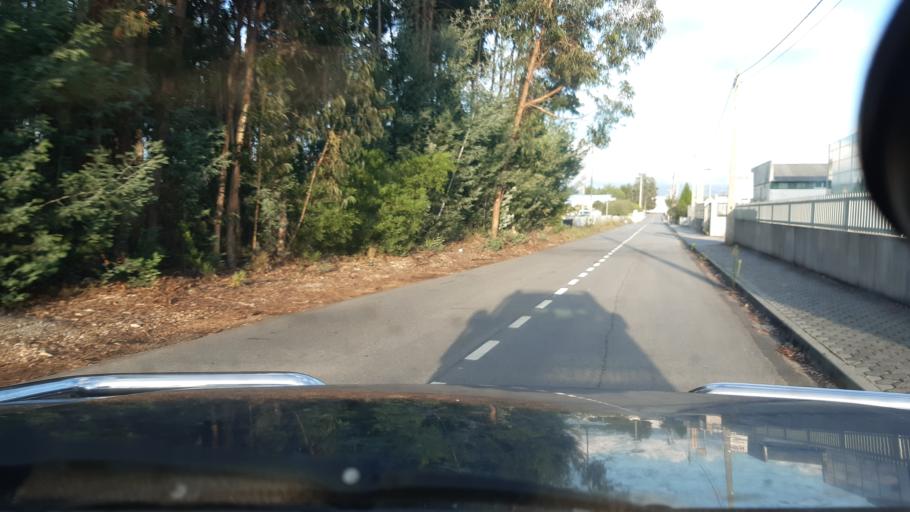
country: PT
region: Aveiro
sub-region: Agueda
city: Agueda
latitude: 40.5819
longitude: -8.4688
